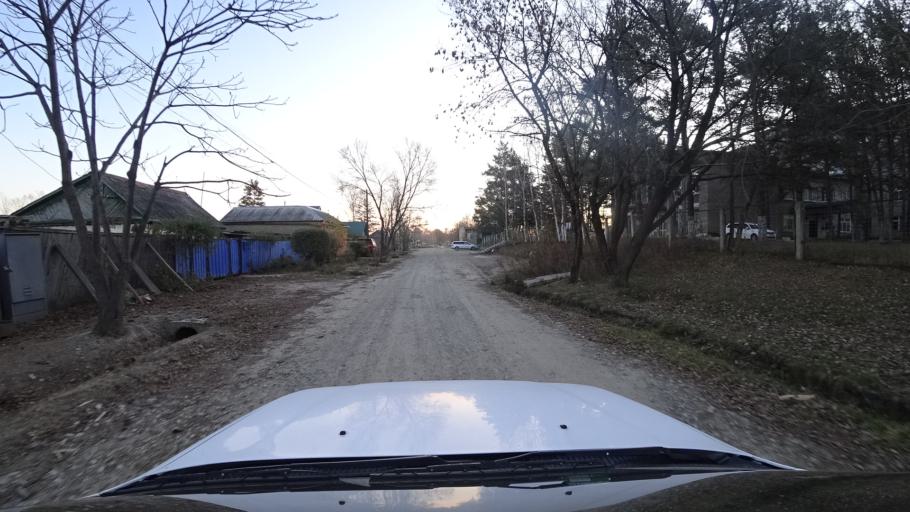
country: RU
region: Primorskiy
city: Dal'nerechensk
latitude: 45.9216
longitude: 133.7366
